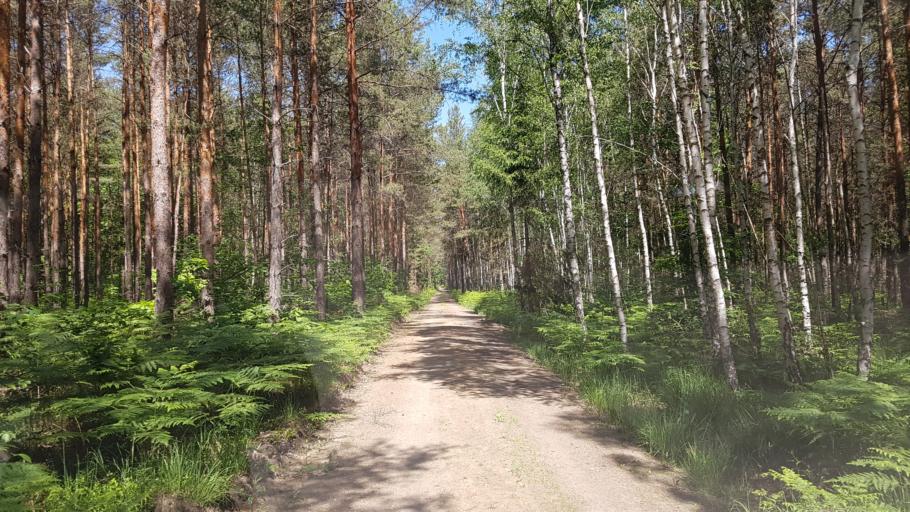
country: DE
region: Brandenburg
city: Hohenleipisch
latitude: 51.5298
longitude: 13.5777
